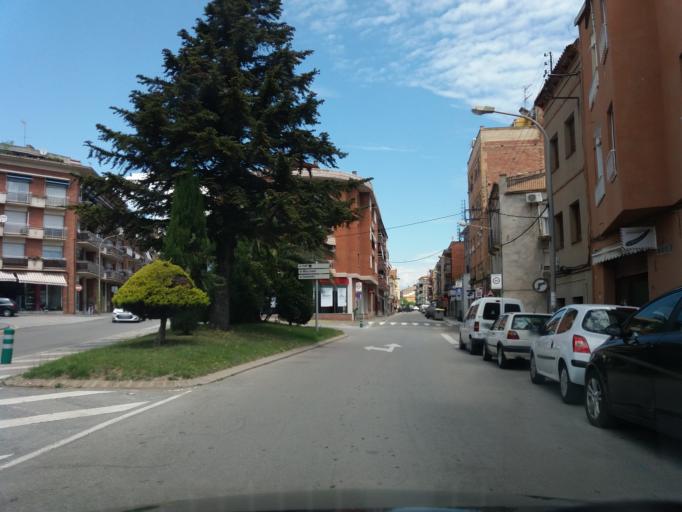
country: ES
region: Catalonia
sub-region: Provincia de Barcelona
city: Sant Joan de Vilatorrada
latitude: 41.7409
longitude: 1.8045
